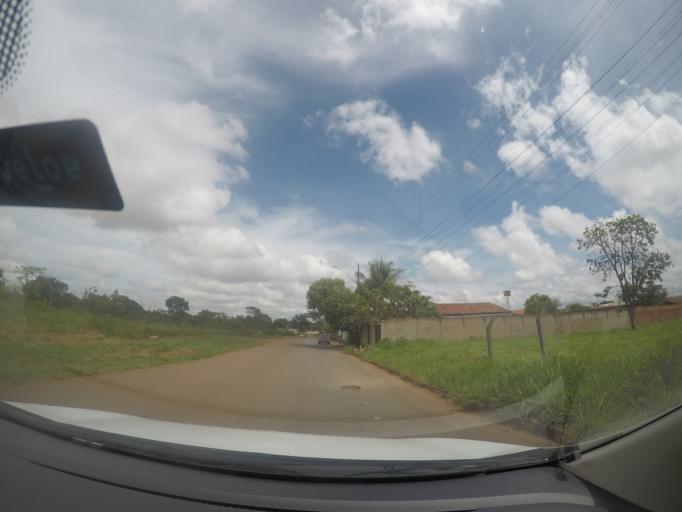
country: BR
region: Goias
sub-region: Goiania
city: Goiania
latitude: -16.7030
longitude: -49.3338
